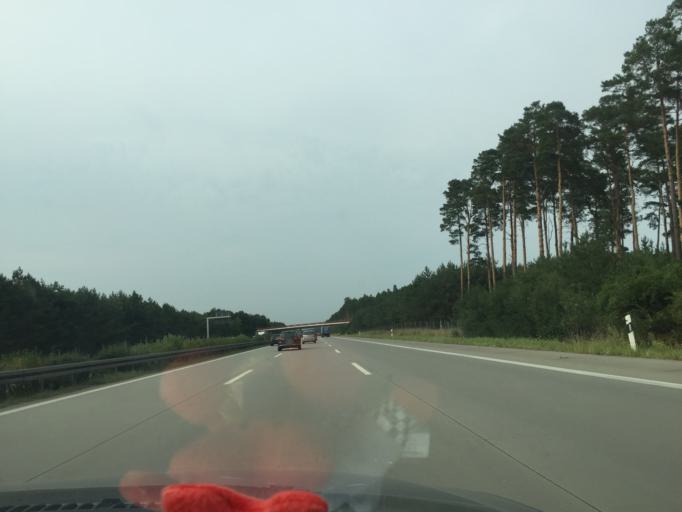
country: DE
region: Brandenburg
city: Grunheide
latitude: 52.3971
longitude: 13.7866
